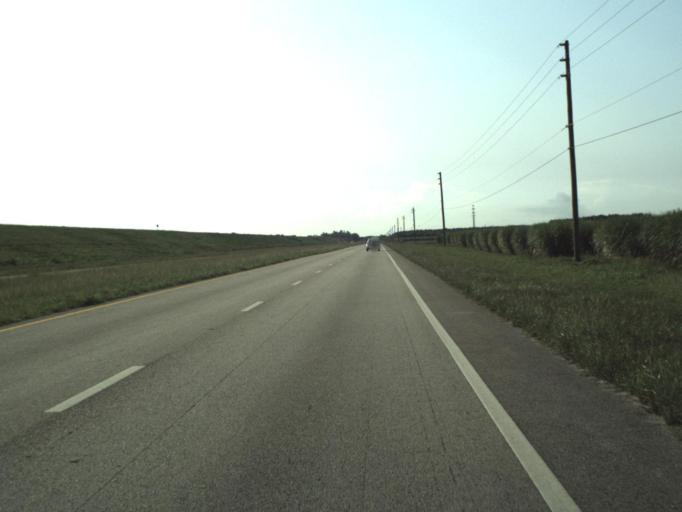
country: US
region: Florida
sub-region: Hendry County
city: Clewiston
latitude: 26.7109
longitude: -80.8352
